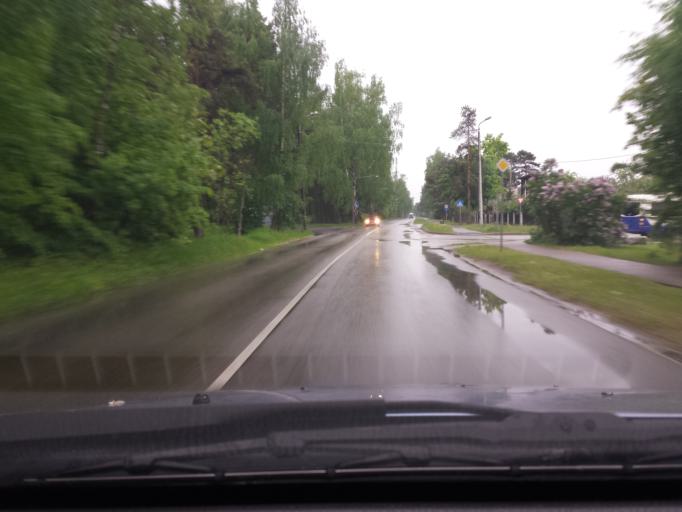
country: LV
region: Riga
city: Bolderaja
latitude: 57.0599
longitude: 24.1061
